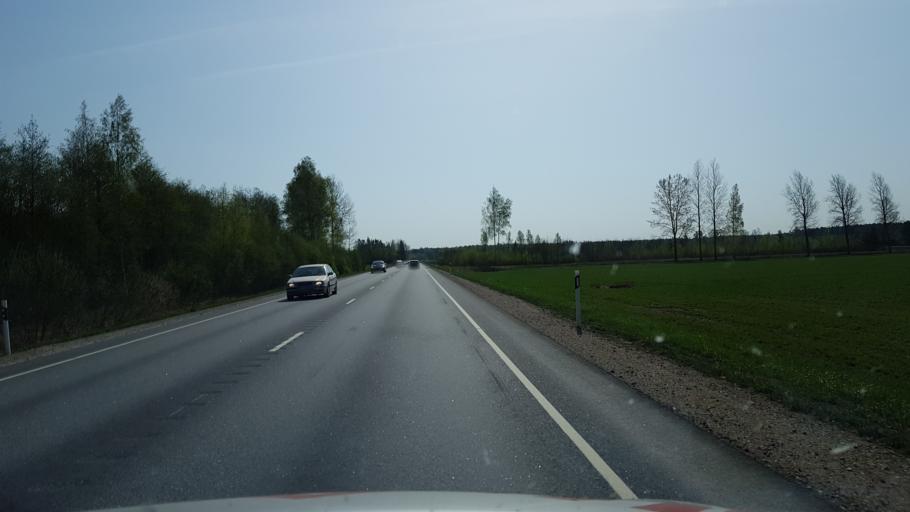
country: EE
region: Paernumaa
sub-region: Paikuse vald
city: Paikuse
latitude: 58.2664
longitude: 24.6485
